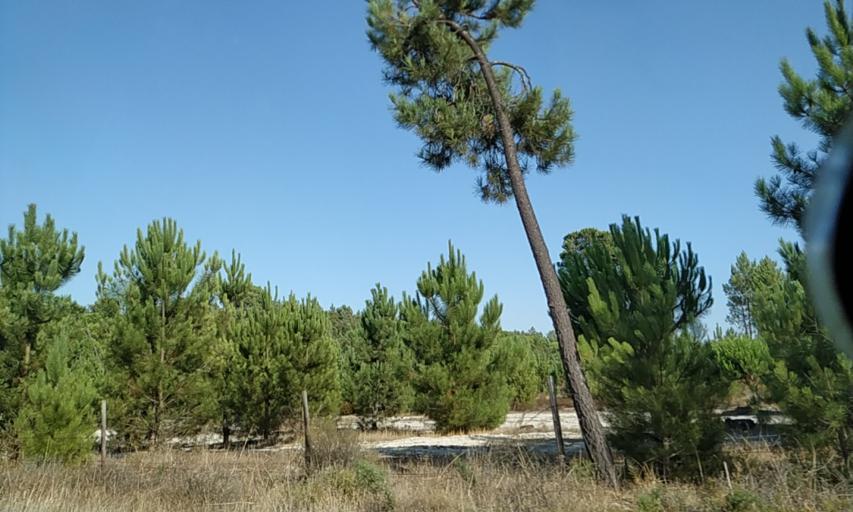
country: PT
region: Santarem
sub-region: Coruche
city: Coruche
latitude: 38.9021
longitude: -8.5294
